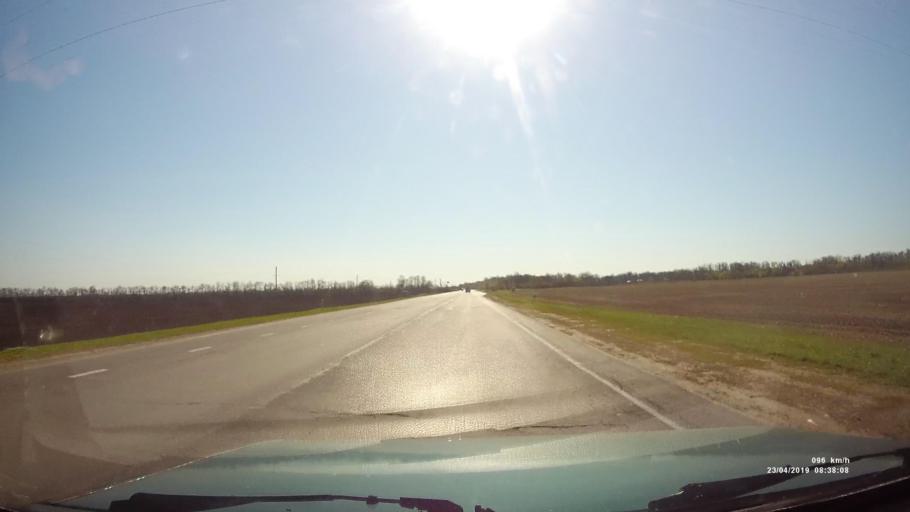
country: RU
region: Rostov
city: Tselina
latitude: 46.5316
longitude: 41.1817
